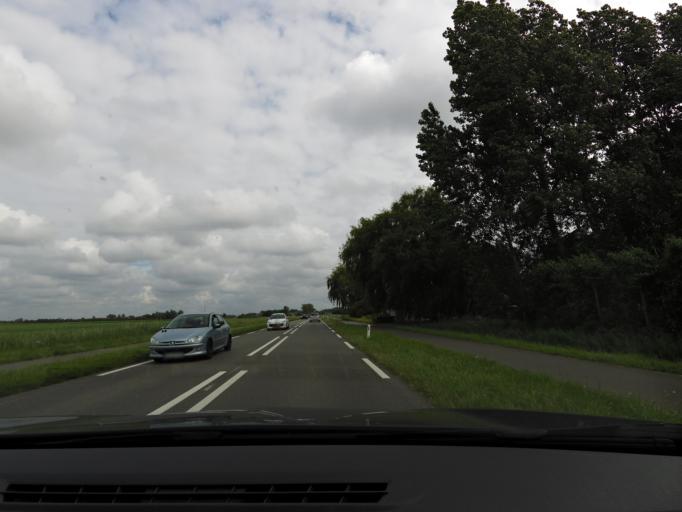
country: NL
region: Zeeland
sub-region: Gemeente Middelburg
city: Middelburg
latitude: 51.5626
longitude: 3.5775
